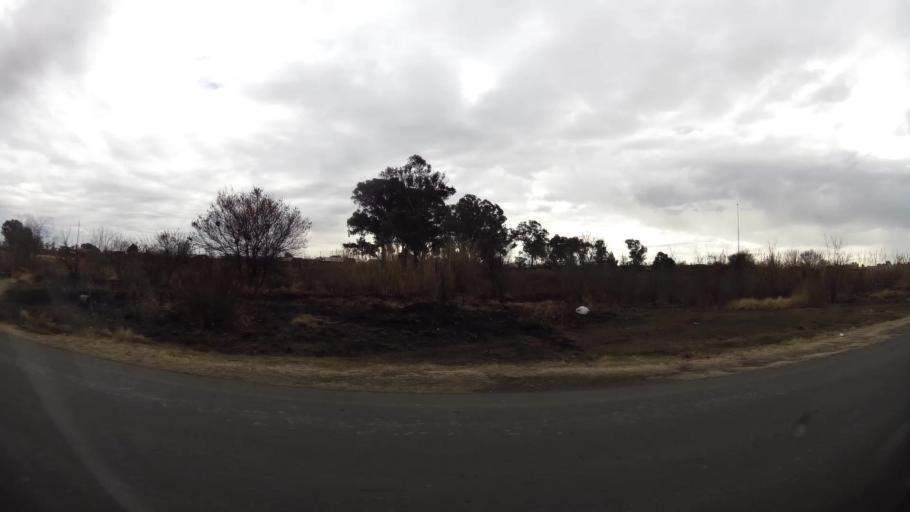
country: ZA
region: Orange Free State
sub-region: Fezile Dabi District Municipality
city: Kroonstad
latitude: -27.6521
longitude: 27.2267
